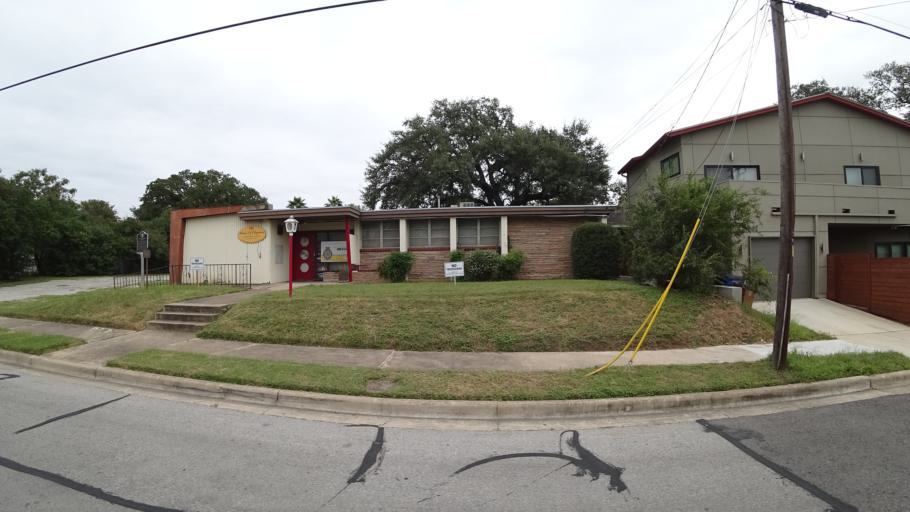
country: US
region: Texas
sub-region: Travis County
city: Austin
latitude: 30.2716
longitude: -97.7276
